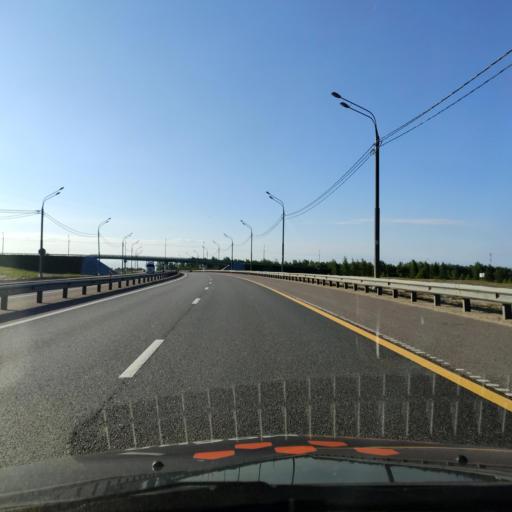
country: RU
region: Lipetsk
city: Khlevnoye
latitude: 52.2402
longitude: 39.0699
